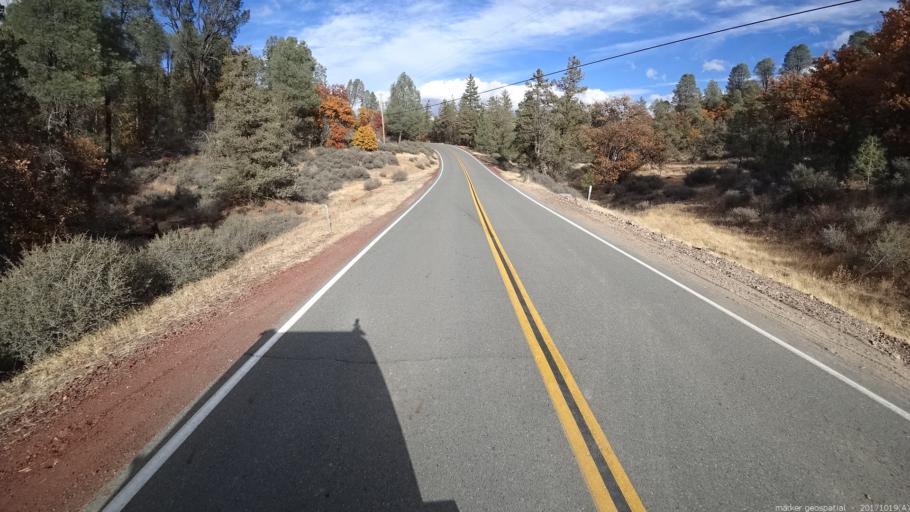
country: US
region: California
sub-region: Shasta County
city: Burney
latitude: 40.9877
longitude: -121.4310
